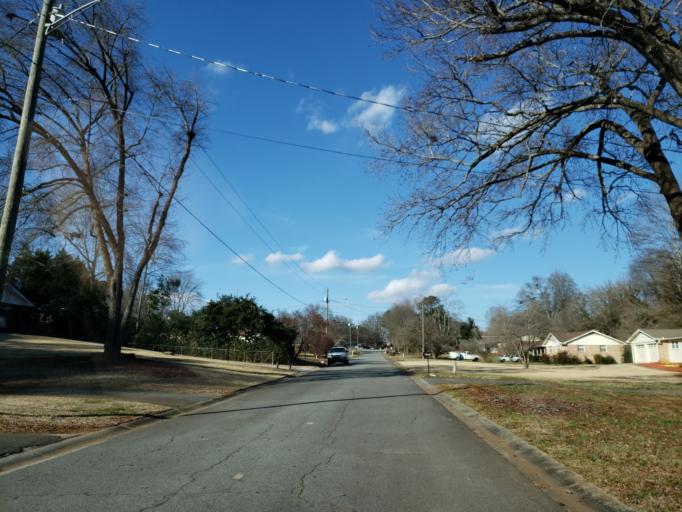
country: US
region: Georgia
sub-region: Cobb County
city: Marietta
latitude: 33.9925
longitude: -84.5196
